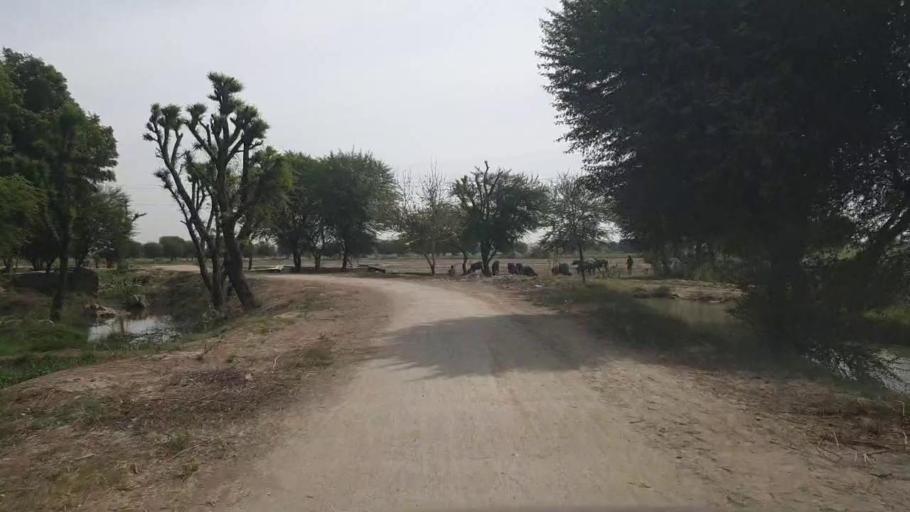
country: PK
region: Sindh
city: Umarkot
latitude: 25.2323
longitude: 69.6982
